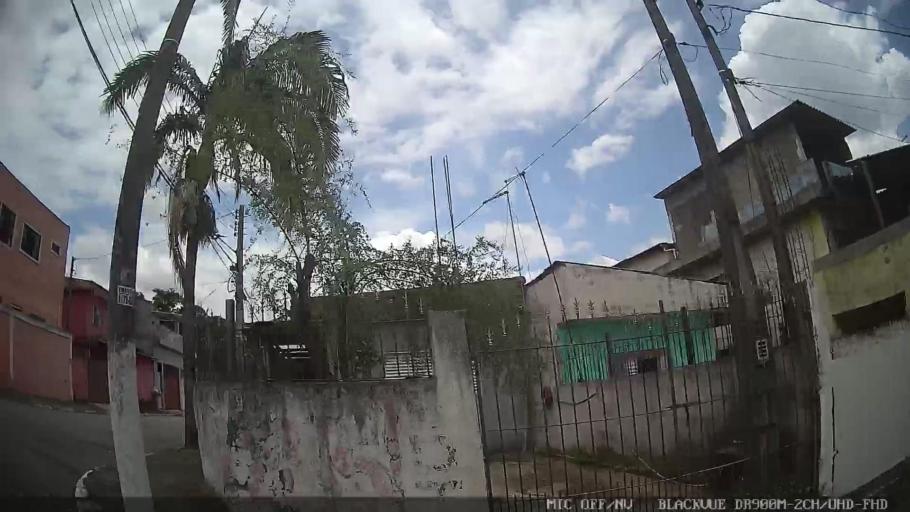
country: BR
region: Sao Paulo
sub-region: Aruja
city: Aruja
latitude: -23.4205
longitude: -46.3699
